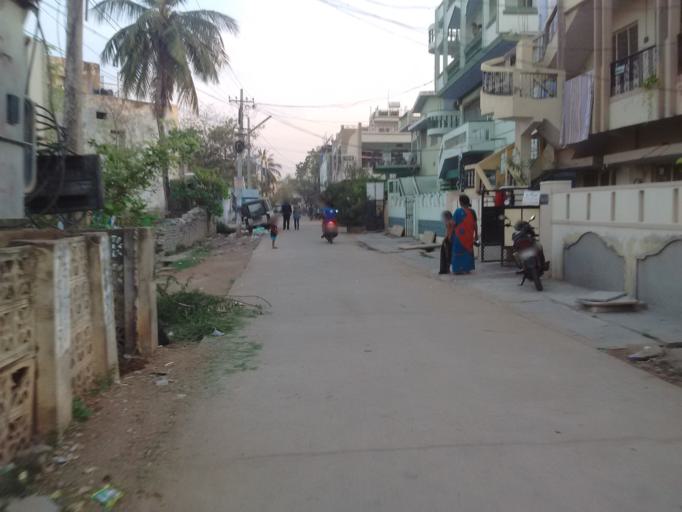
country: IN
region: Telangana
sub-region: Mahbubnagar
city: Alampur
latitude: 15.8114
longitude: 78.0423
